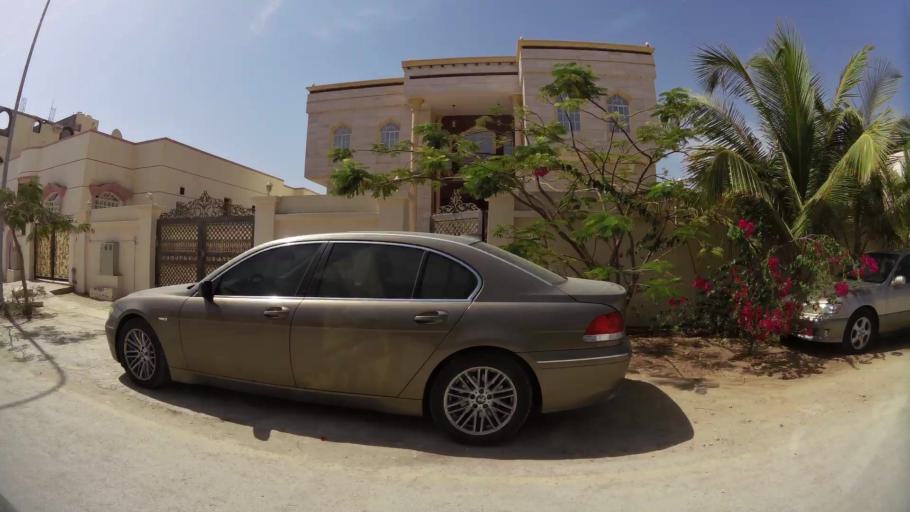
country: OM
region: Zufar
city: Salalah
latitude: 17.0399
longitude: 54.1588
